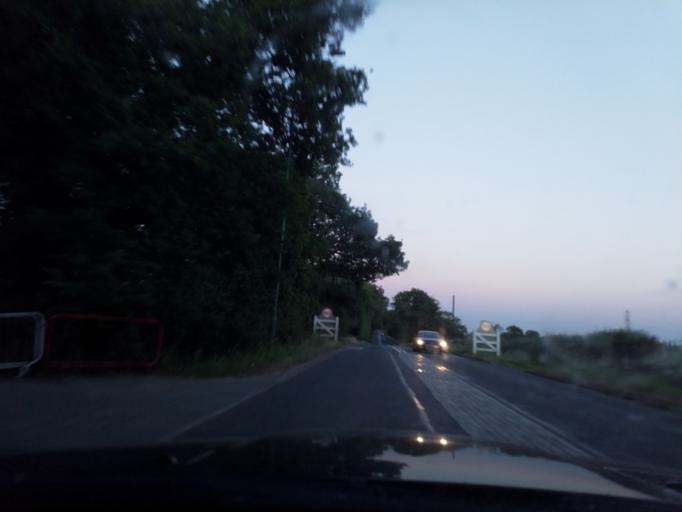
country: GB
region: England
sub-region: Solihull
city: Balsall Common
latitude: 52.3802
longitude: -1.6405
